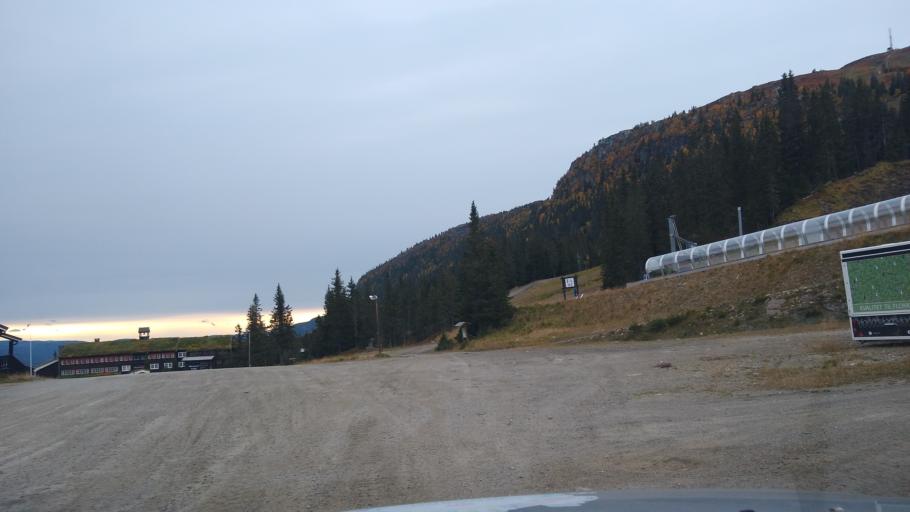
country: NO
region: Oppland
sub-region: Ringebu
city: Ringebu
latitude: 61.4726
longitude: 10.1344
